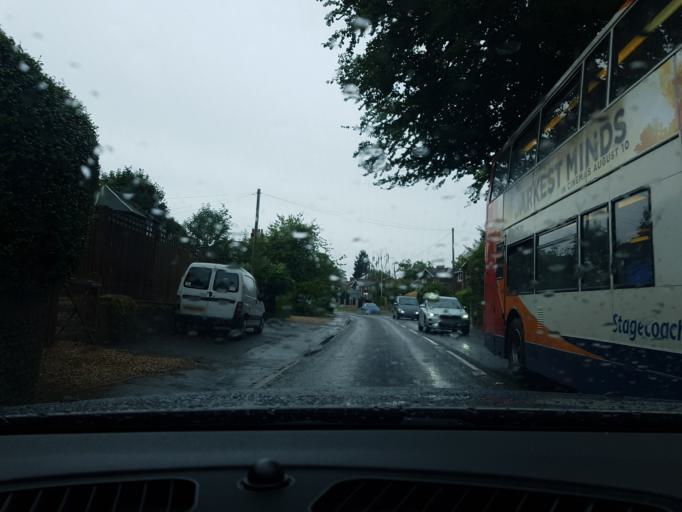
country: GB
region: England
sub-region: Surrey
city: Hale
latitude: 51.2288
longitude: -0.7852
